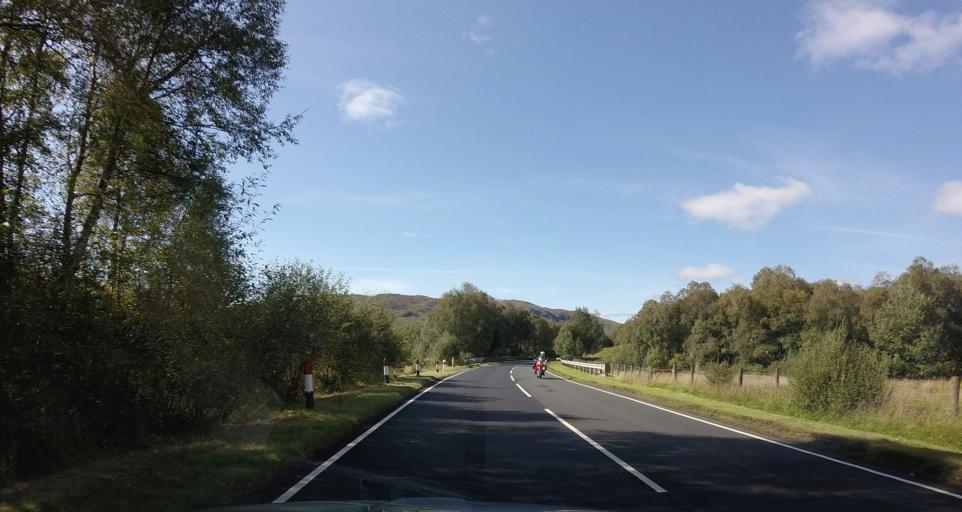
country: GB
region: Scotland
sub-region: Stirling
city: Callander
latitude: 56.4210
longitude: -4.4266
